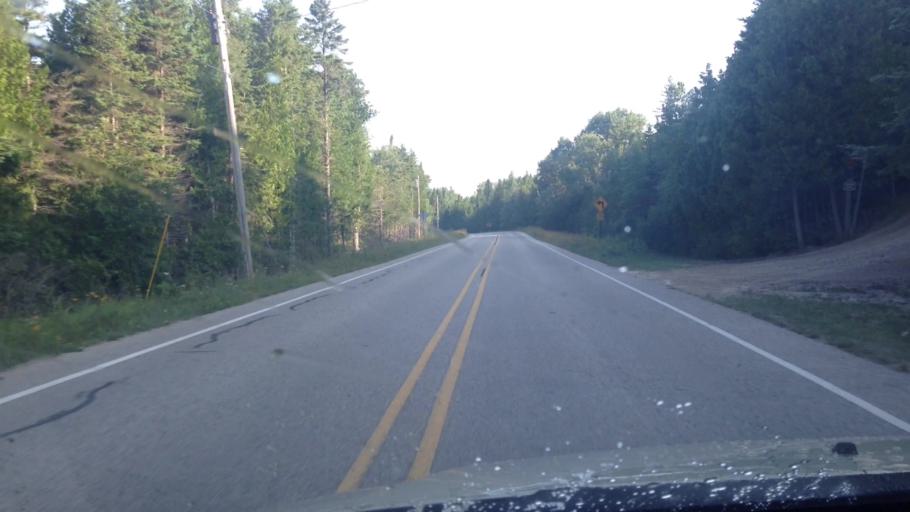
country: US
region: Michigan
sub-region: Mackinac County
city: Saint Ignace
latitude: 45.8901
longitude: -84.7653
